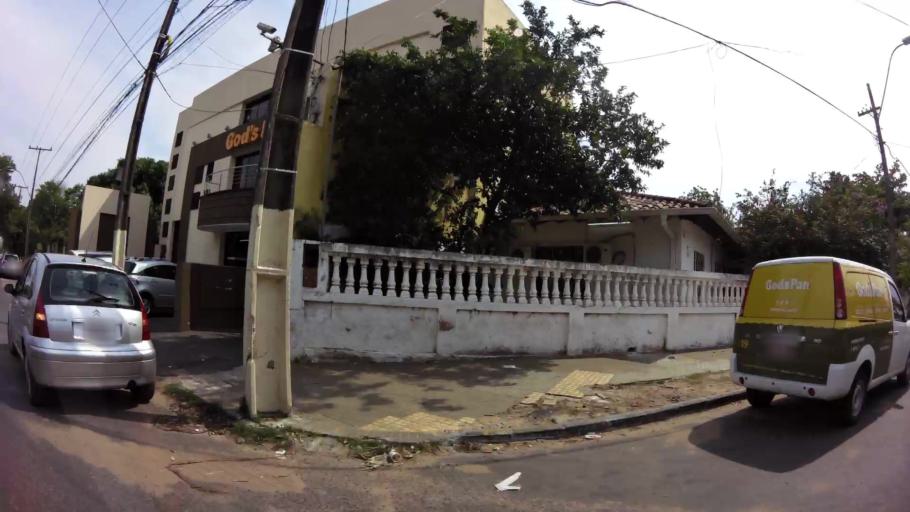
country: PY
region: Asuncion
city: Asuncion
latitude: -25.2577
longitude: -57.5817
